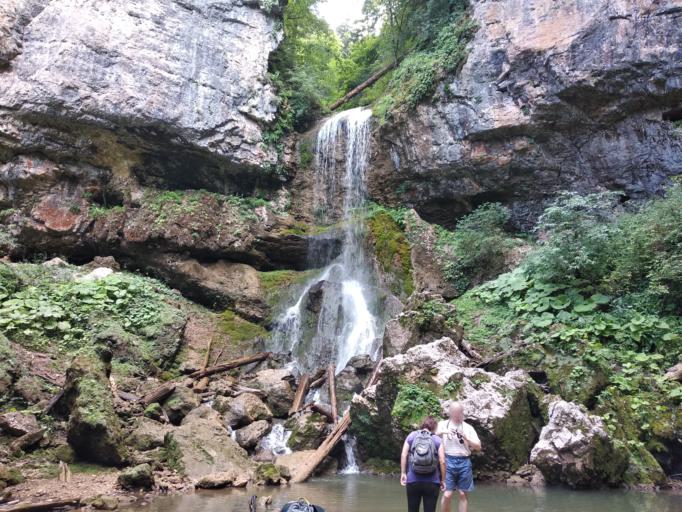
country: RU
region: Adygeya
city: Kamennomostskiy
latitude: 44.1991
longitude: 40.0380
